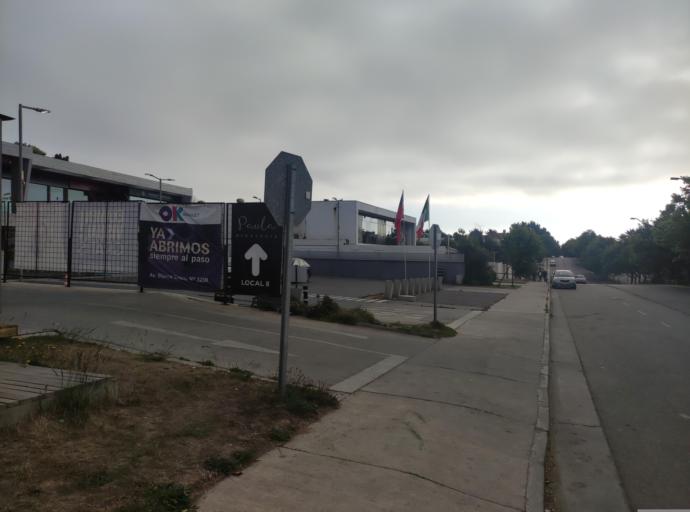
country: CL
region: Valparaiso
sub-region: Provincia de Valparaiso
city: Vina del Mar
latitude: -32.9424
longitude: -71.5338
